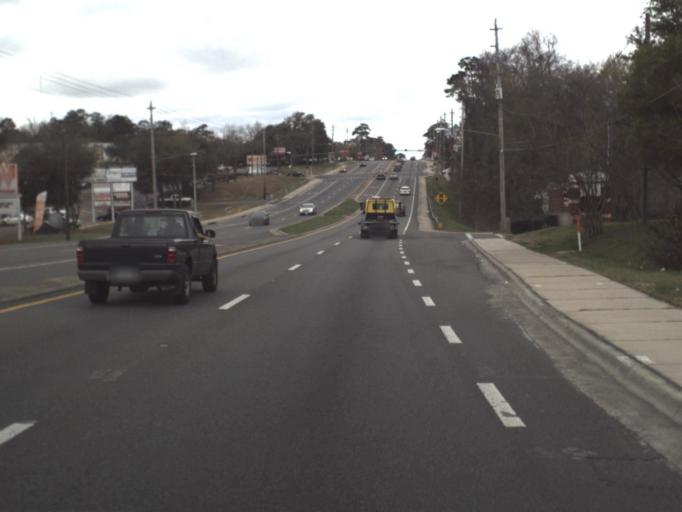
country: US
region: Florida
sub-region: Leon County
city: Tallahassee
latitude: 30.4277
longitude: -84.2374
